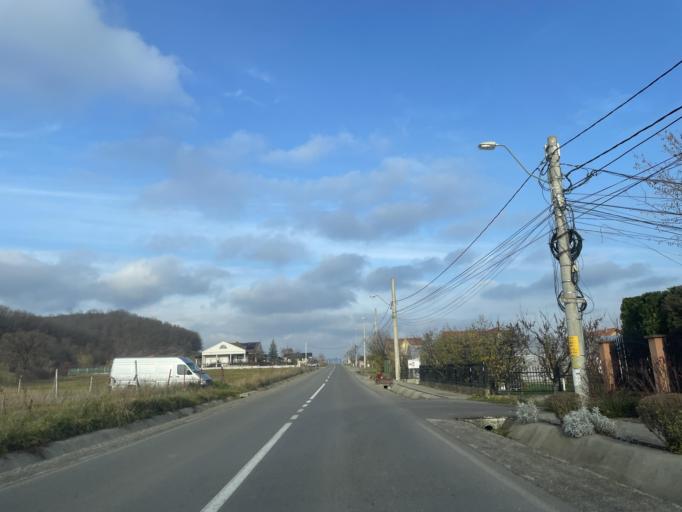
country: RO
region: Mures
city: Reghin-Sat
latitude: 46.7930
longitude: 24.7044
